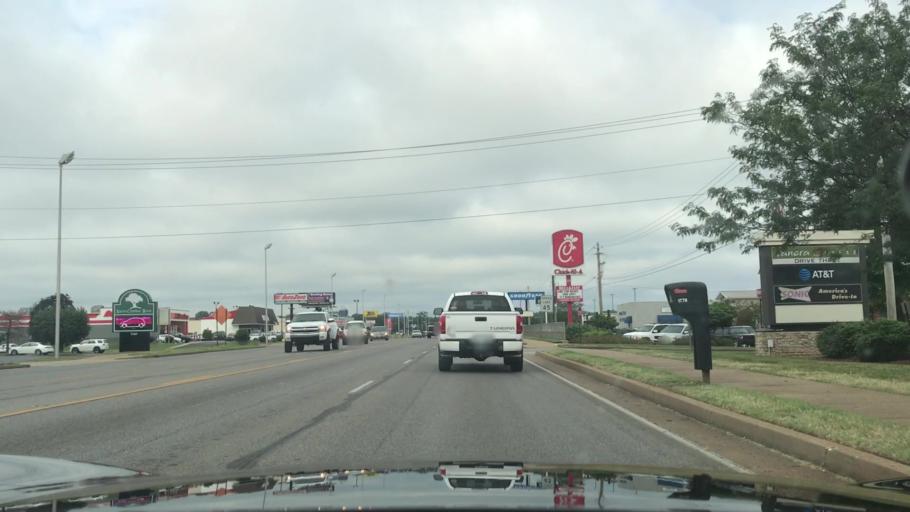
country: US
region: Kentucky
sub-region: Warren County
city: Bowling Green
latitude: 36.9531
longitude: -86.4319
